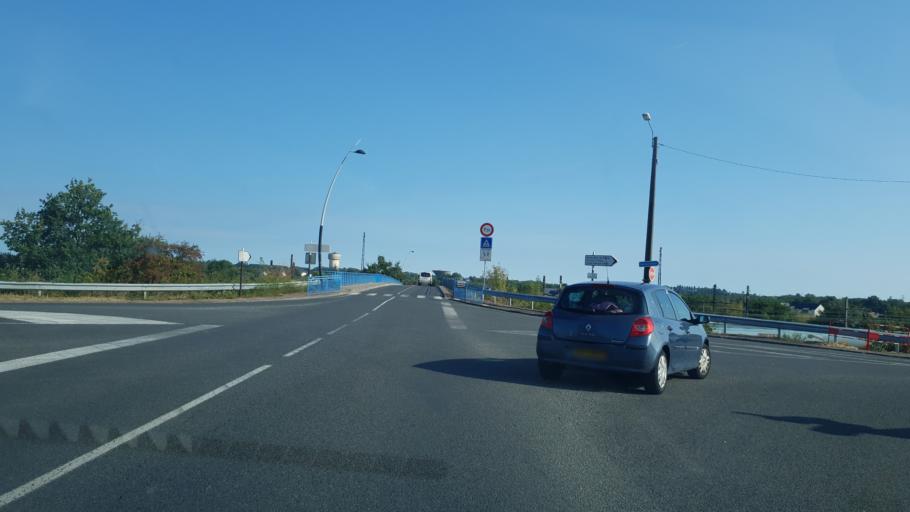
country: FR
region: Centre
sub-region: Departement d'Indre-et-Loire
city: La Ville-aux-Dames
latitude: 47.3903
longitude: 0.7698
